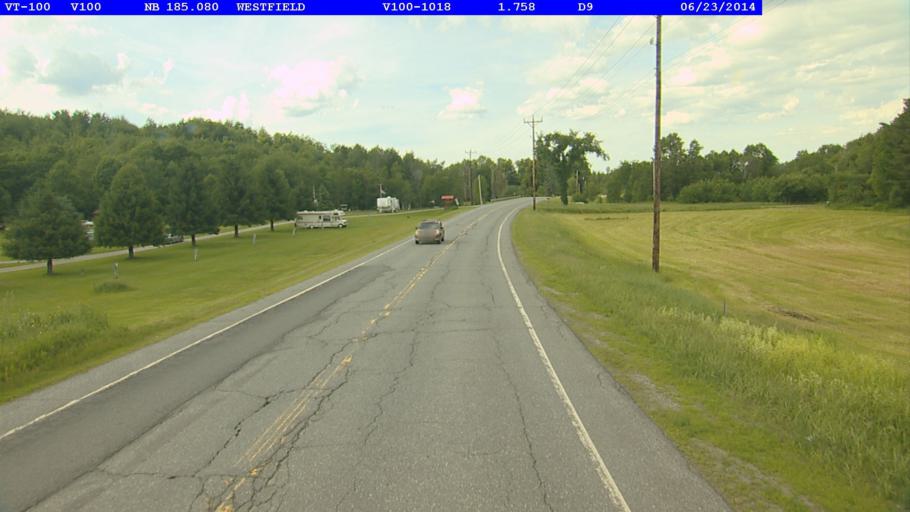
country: US
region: Vermont
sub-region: Orleans County
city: Newport
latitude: 44.8602
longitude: -72.4344
